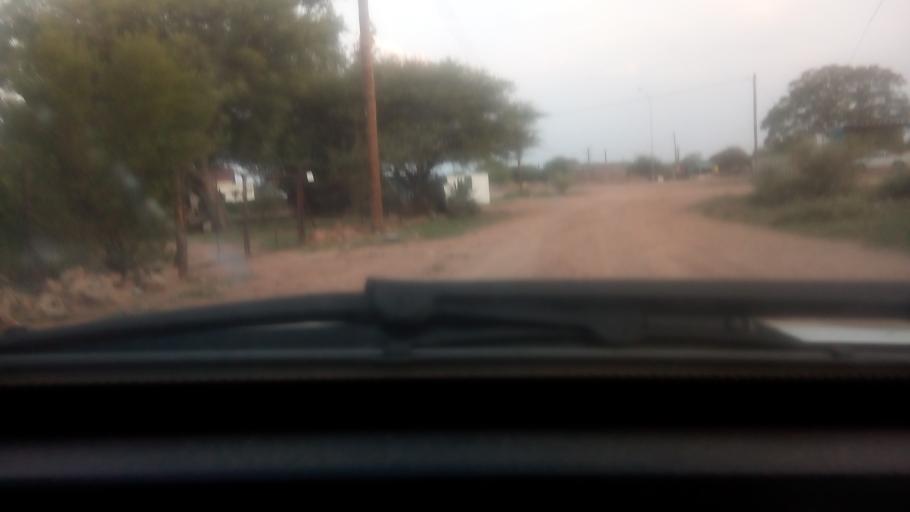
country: BW
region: Kgatleng
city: Bokaa
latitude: -24.4278
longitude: 26.0204
